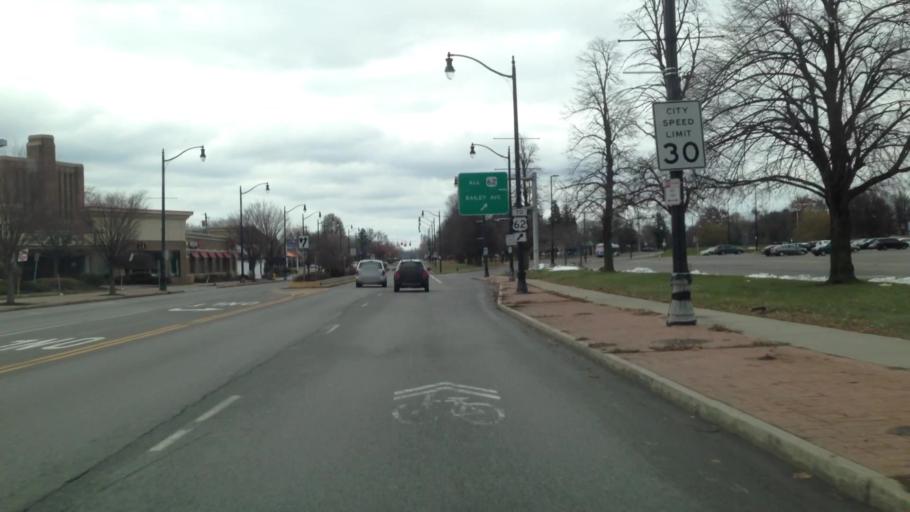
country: US
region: New York
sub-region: Erie County
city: Eggertsville
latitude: 42.9580
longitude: -78.8173
